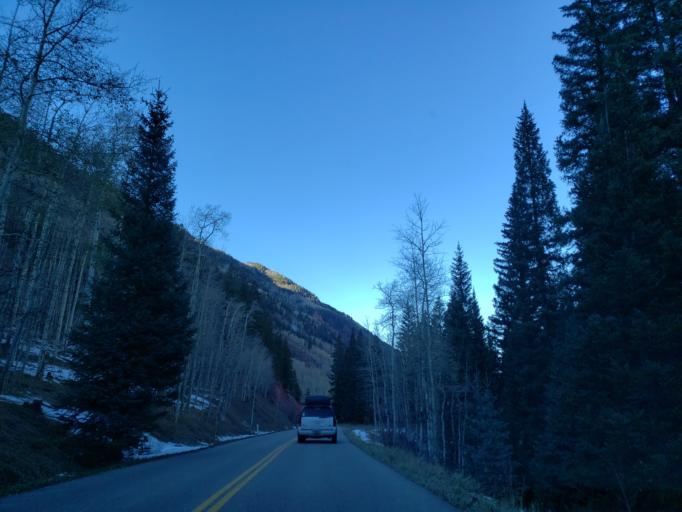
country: US
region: Colorado
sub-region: Pitkin County
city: Snowmass Village
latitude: 39.1320
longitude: -106.9020
